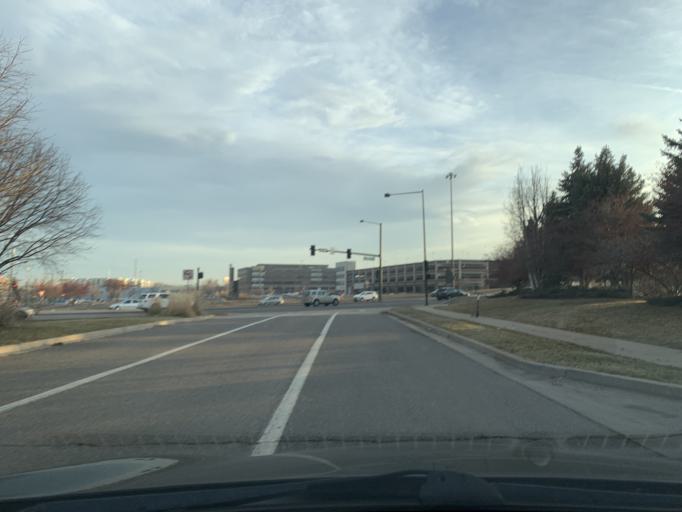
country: US
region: Colorado
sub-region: Denver County
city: Denver
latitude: 39.7454
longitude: -105.0101
